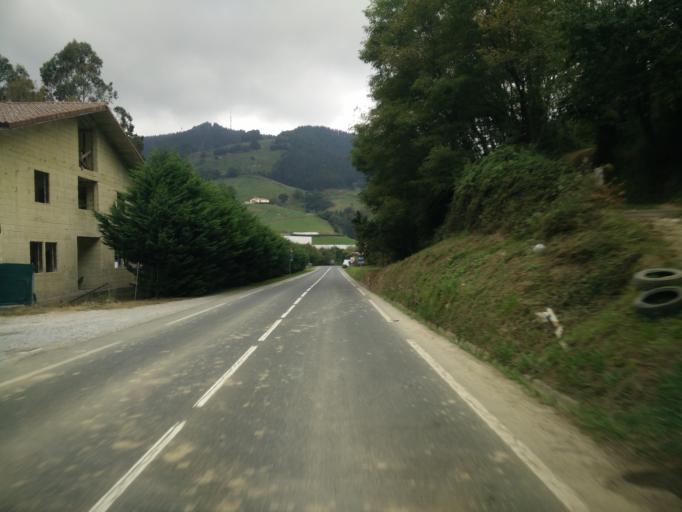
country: ES
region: Basque Country
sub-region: Bizkaia
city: Ondarroa
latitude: 43.3089
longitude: -2.4059
